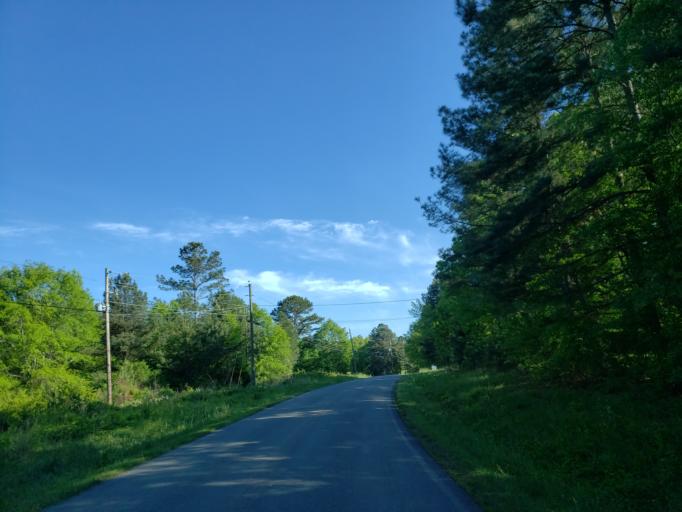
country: US
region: Georgia
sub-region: Polk County
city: Aragon
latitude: 34.0157
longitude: -85.1455
